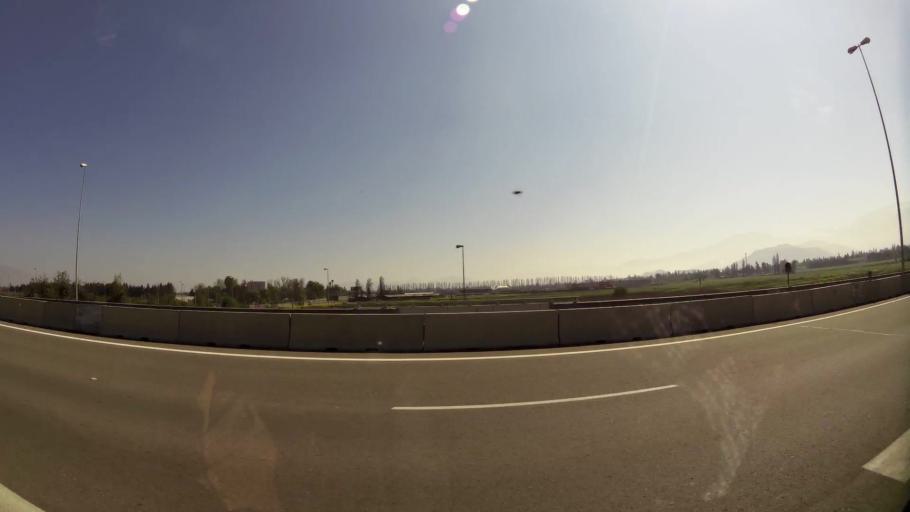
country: CL
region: Santiago Metropolitan
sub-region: Provincia de Chacabuco
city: Chicureo Abajo
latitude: -33.2916
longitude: -70.7004
